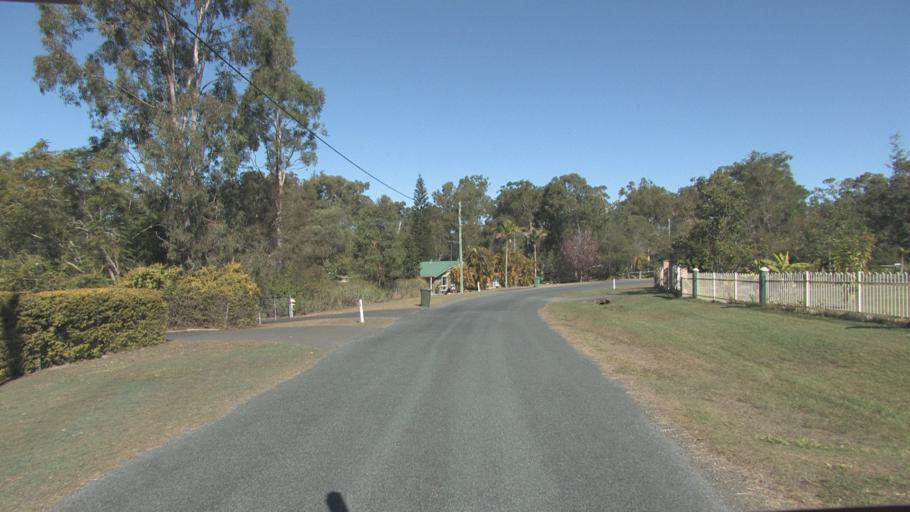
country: AU
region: Queensland
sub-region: Logan
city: Park Ridge South
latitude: -27.7287
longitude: 153.0473
